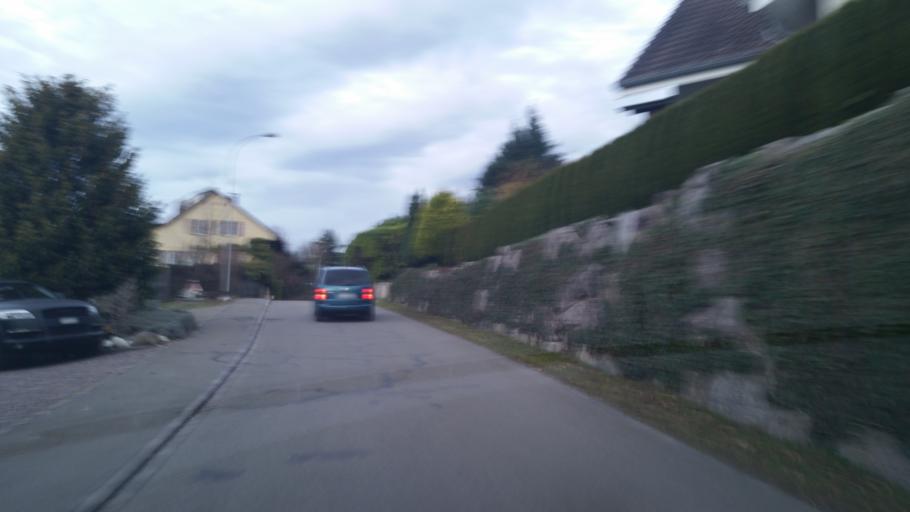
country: CH
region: Aargau
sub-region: Bezirk Baden
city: Kunten
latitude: 47.3891
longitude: 8.3270
